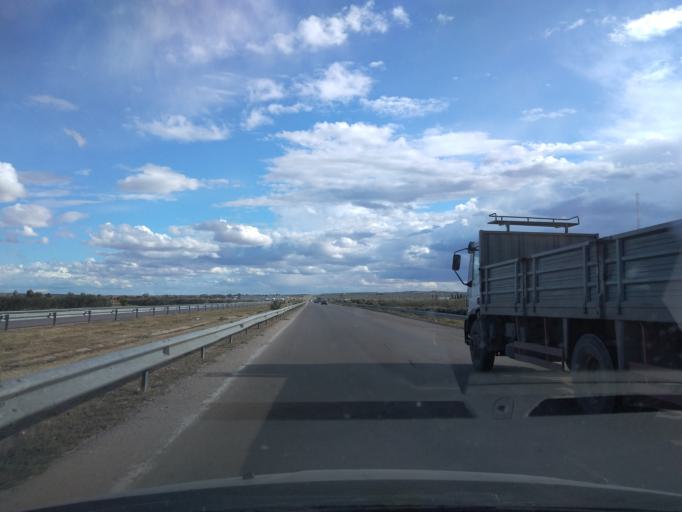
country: TN
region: Al Munastir
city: Manzil Kamil
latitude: 35.5815
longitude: 10.6082
